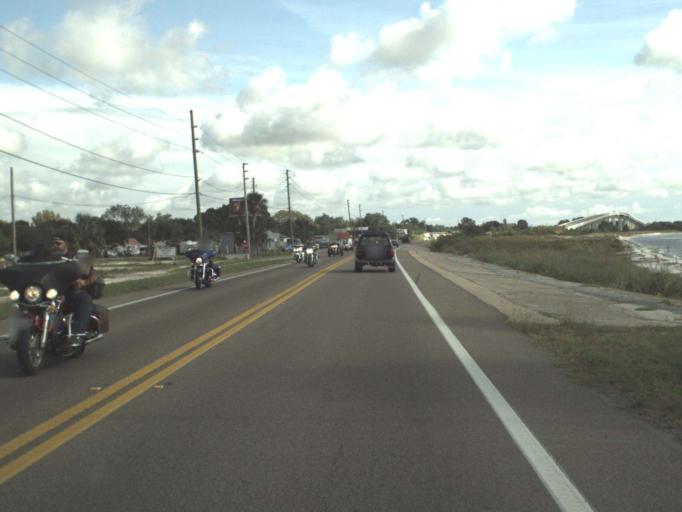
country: US
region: Florida
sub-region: Gulf County
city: Port Saint Joe
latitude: 29.8414
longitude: -85.3201
